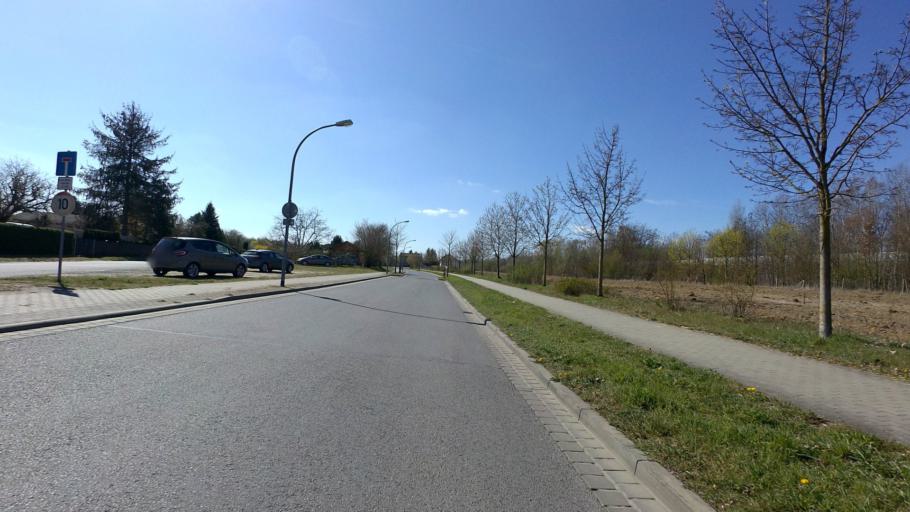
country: DE
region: Brandenburg
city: Grossbeeren
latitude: 52.3913
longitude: 13.3026
